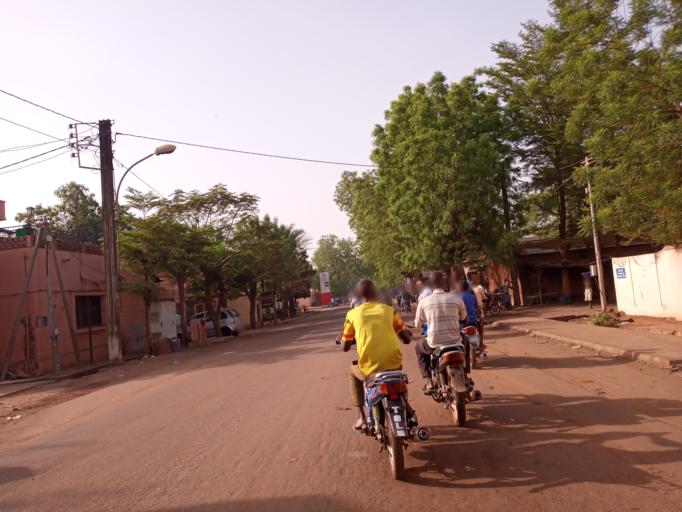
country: ML
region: Bamako
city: Bamako
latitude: 12.6594
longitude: -7.9810
